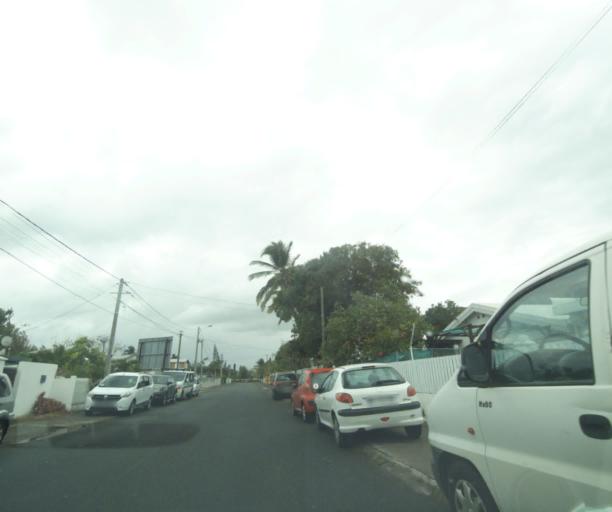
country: RE
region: Reunion
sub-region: Reunion
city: Saint-Paul
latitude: -20.9980
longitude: 55.2804
